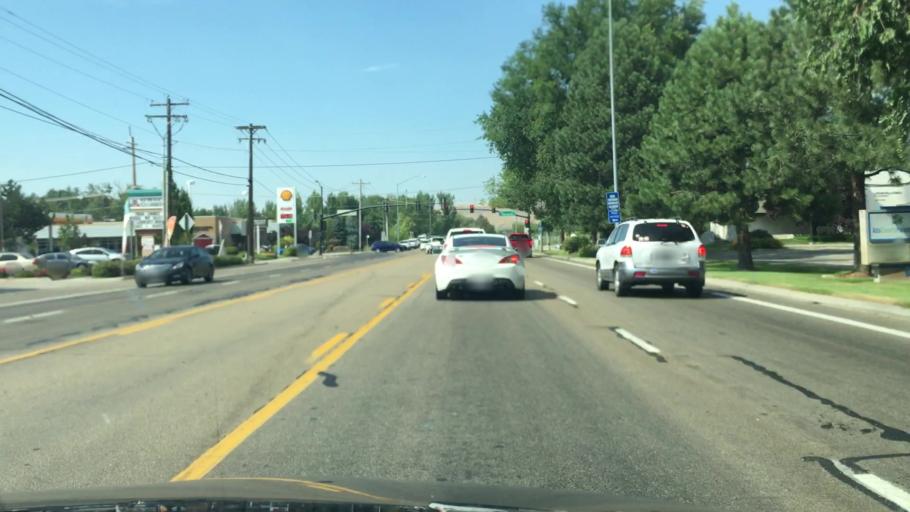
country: US
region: Idaho
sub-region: Ada County
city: Garden City
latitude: 43.6581
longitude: -116.2797
